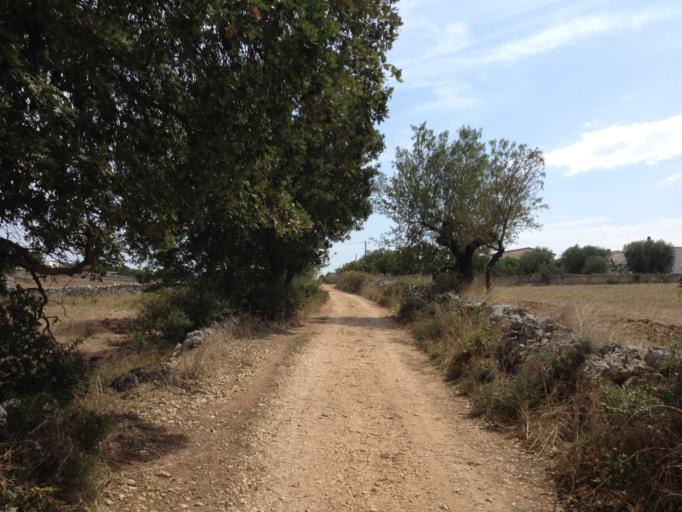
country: IT
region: Apulia
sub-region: Provincia di Bari
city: Gioia del Colle
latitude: 40.8240
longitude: 16.9766
